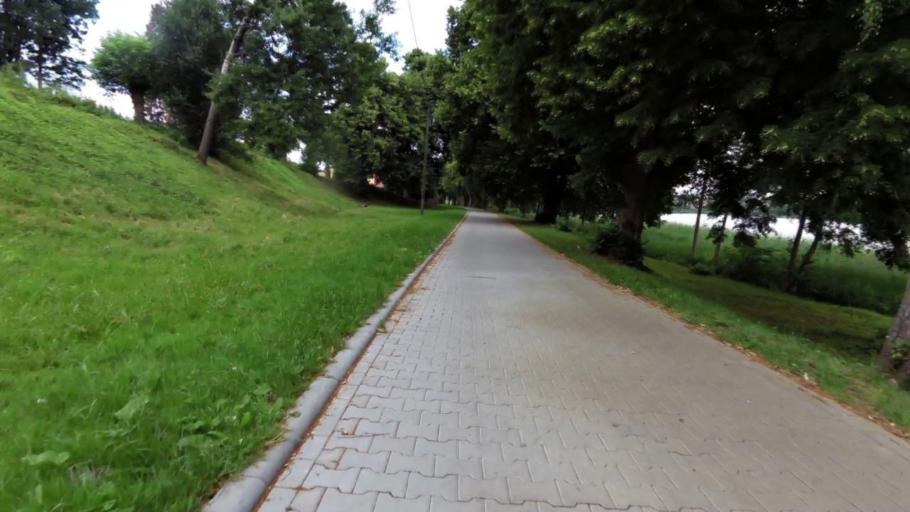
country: PL
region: West Pomeranian Voivodeship
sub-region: Powiat stargardzki
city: Chociwel
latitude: 53.4609
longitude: 15.3383
